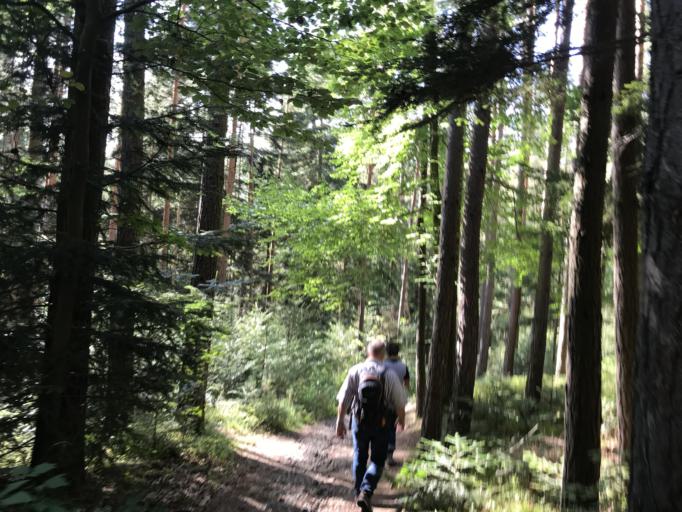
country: DE
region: Baden-Wuerttemberg
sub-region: Karlsruhe Region
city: Bad Teinach-Zavelstein
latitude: 48.7028
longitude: 8.7118
